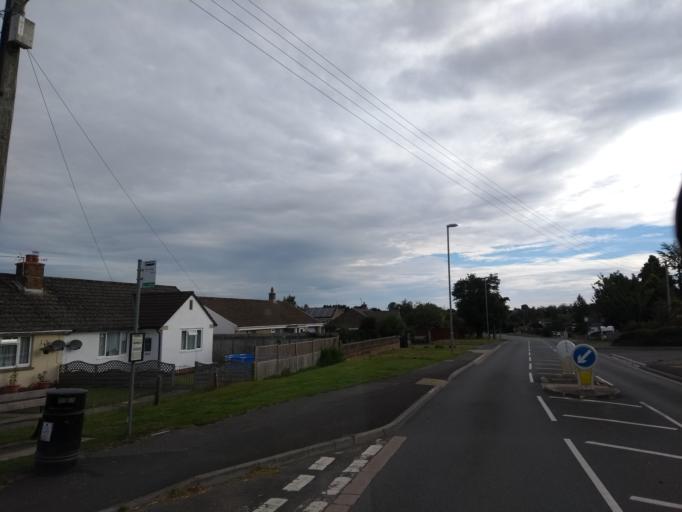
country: GB
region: England
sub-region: Somerset
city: Crewkerne
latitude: 50.8419
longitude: -2.7754
